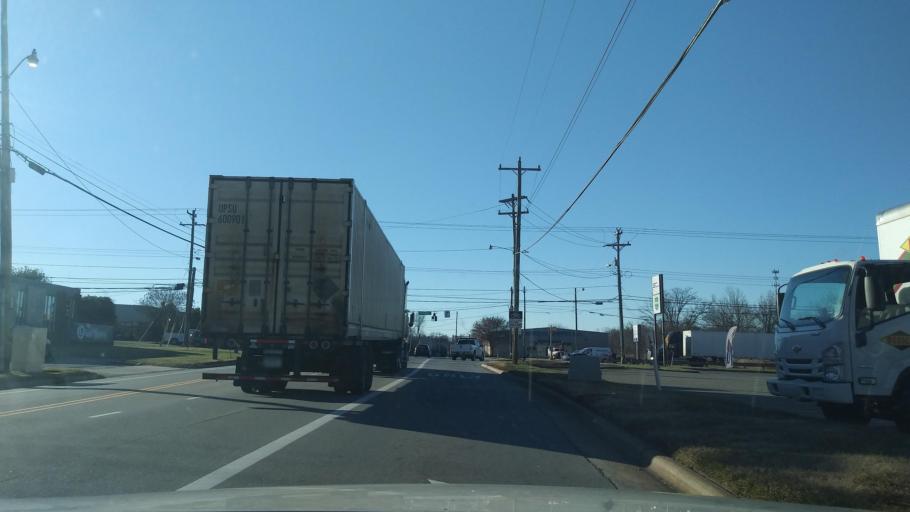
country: US
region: North Carolina
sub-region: Guilford County
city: Greensboro
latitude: 36.0292
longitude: -79.7907
